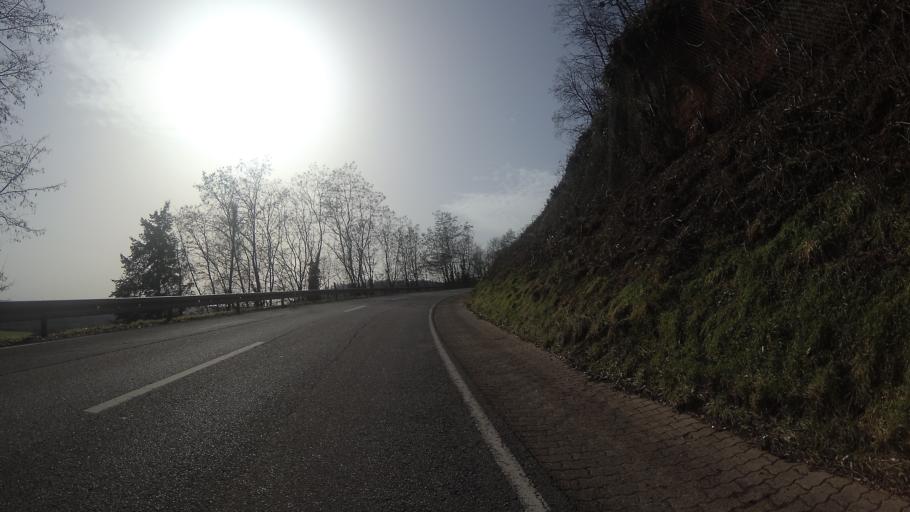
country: DE
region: Saarland
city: Uberherrn
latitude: 49.2695
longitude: 6.7056
